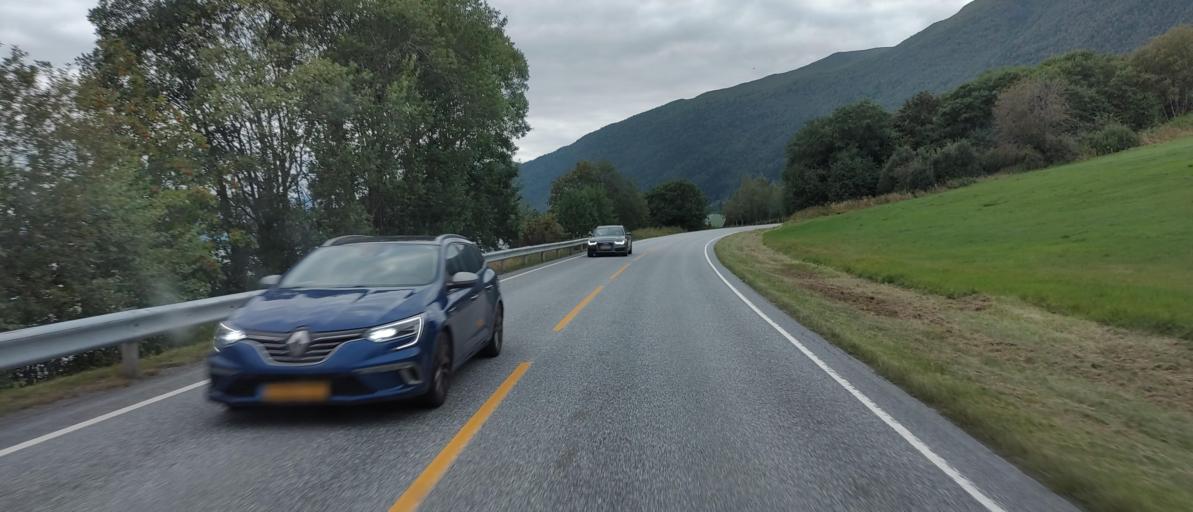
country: NO
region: More og Romsdal
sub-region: Rauma
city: Andalsnes
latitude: 62.5766
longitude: 7.7571
